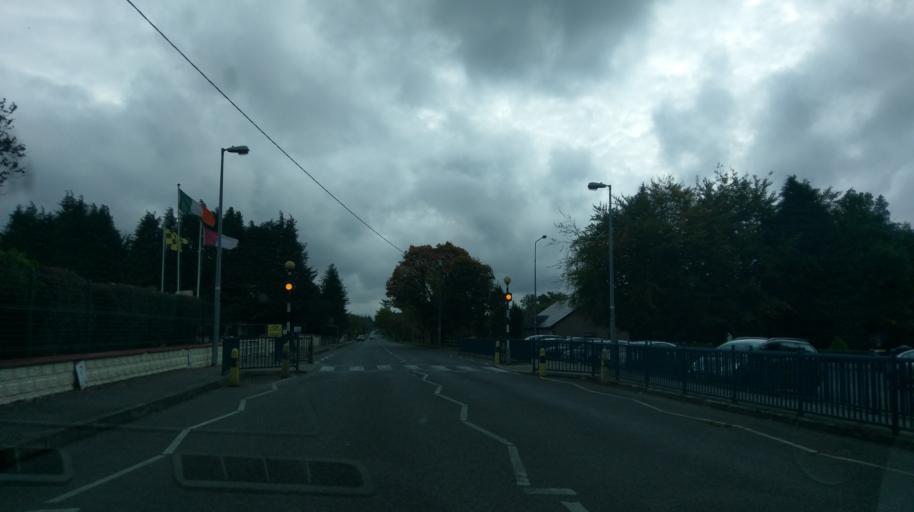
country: IE
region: Connaught
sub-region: County Galway
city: Loughrea
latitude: 53.4678
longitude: -8.4934
